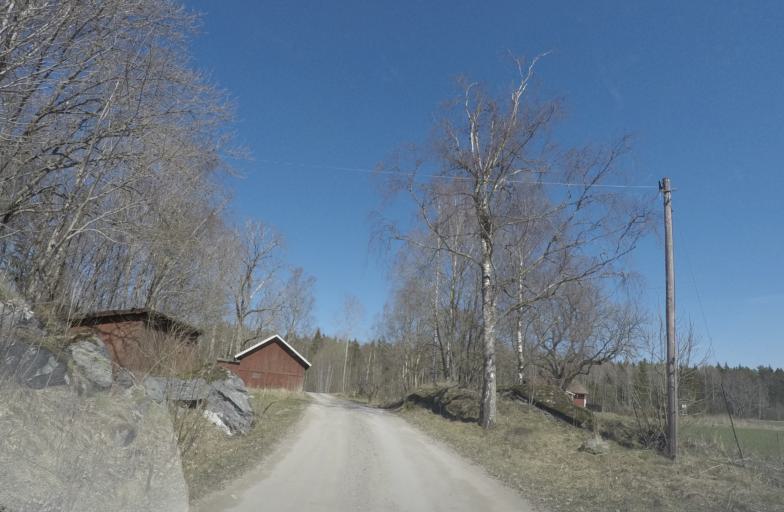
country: SE
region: Vaestmanland
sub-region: Vasteras
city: Vasteras
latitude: 59.6639
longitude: 16.4957
